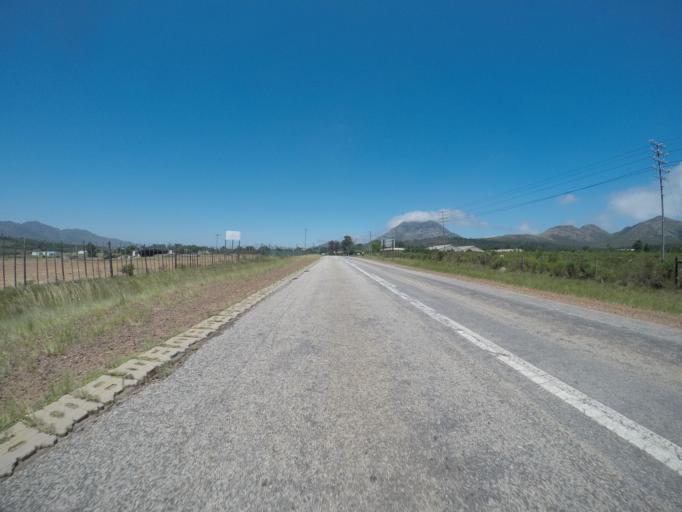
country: ZA
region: Eastern Cape
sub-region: Cacadu District Municipality
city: Kareedouw
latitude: -33.9491
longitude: 24.2803
